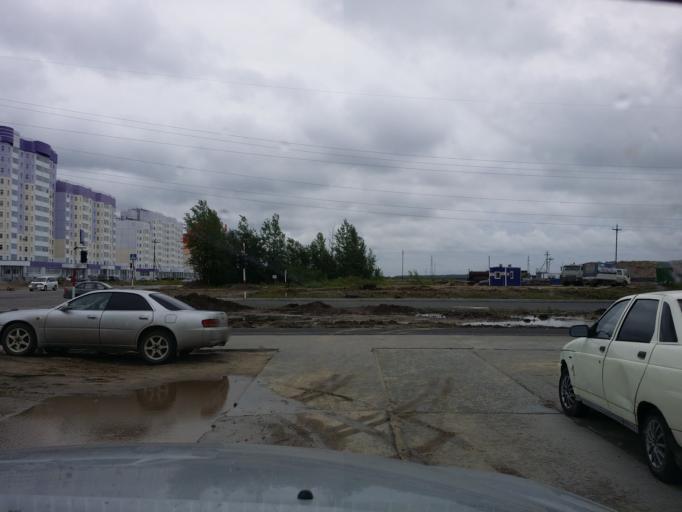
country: RU
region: Khanty-Mansiyskiy Avtonomnyy Okrug
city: Nizhnevartovsk
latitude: 60.9320
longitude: 76.6205
